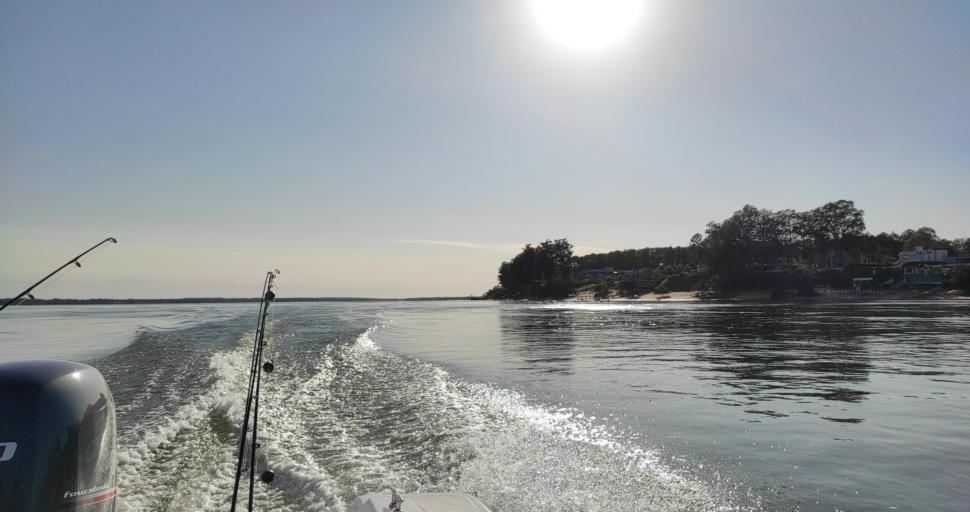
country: AR
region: Corrientes
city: Ituzaingo
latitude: -27.5998
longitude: -56.8177
